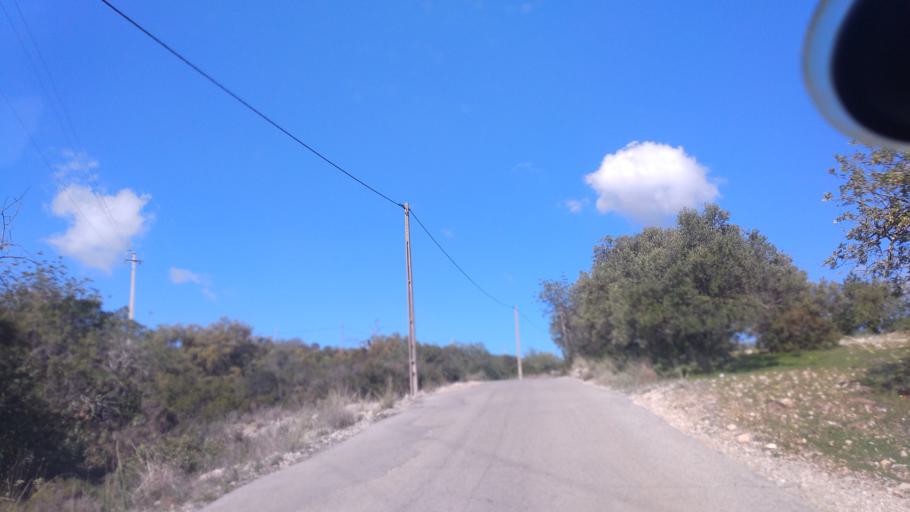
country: PT
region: Faro
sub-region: Sao Bras de Alportel
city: Sao Bras de Alportel
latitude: 37.1348
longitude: -7.9068
